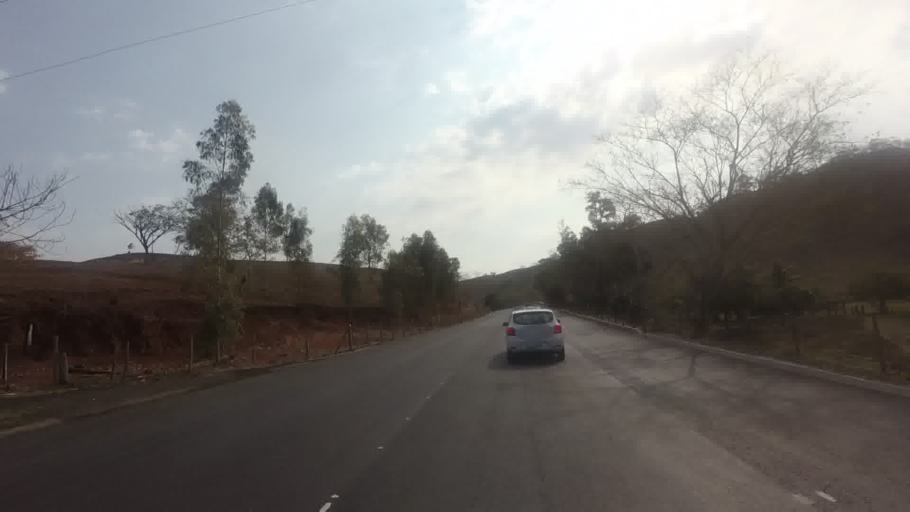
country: BR
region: Rio de Janeiro
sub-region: Bom Jesus Do Itabapoana
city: Bom Jesus do Itabapoana
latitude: -21.1981
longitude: -41.7123
